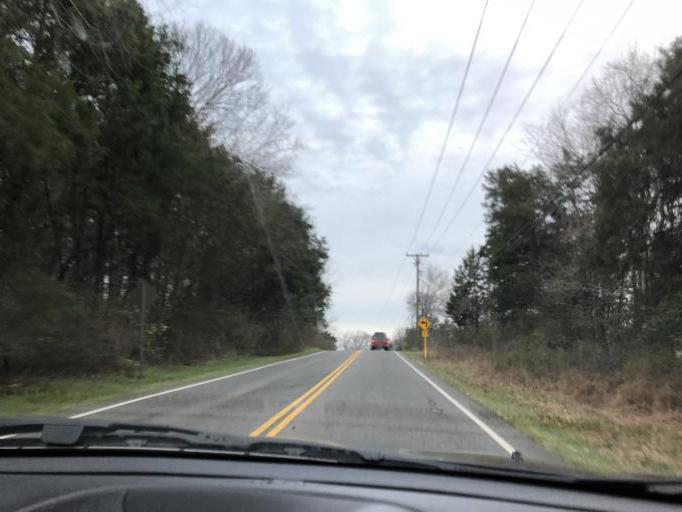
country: US
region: Tennessee
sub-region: Wilson County
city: Green Hill
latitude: 36.1981
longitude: -86.5928
